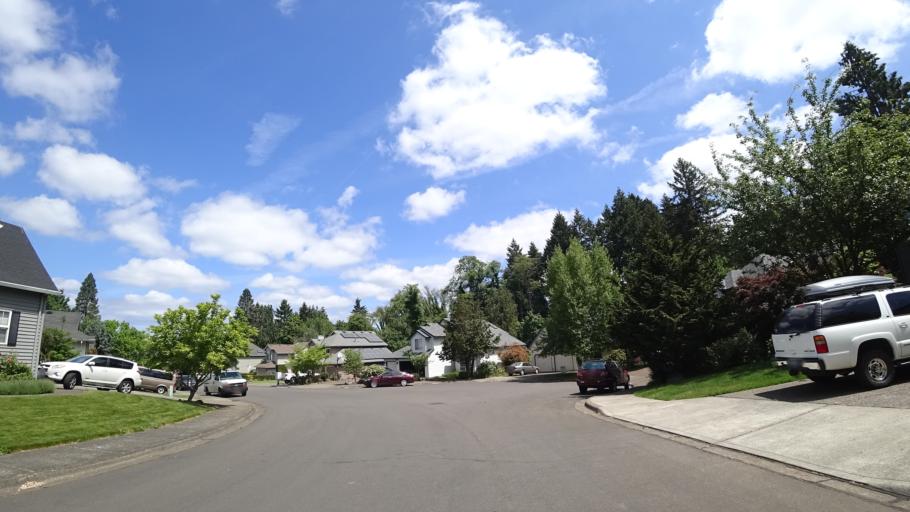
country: US
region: Oregon
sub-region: Washington County
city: Tigard
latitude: 45.4287
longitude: -122.7950
